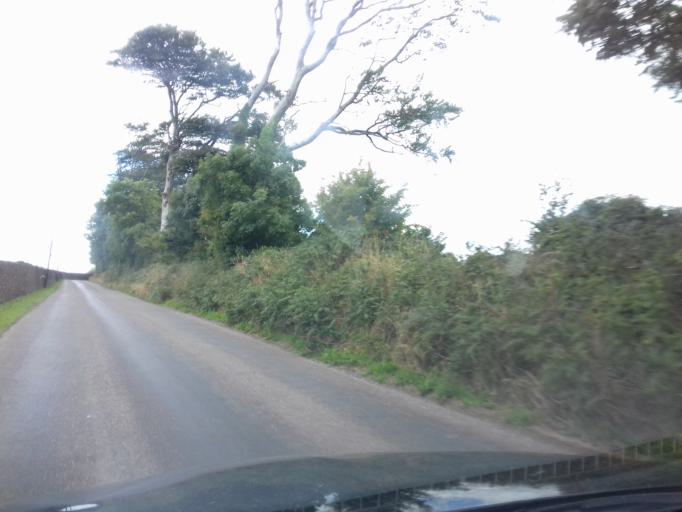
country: IE
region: Munster
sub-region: Waterford
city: Portlaw
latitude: 52.1775
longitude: -7.3480
